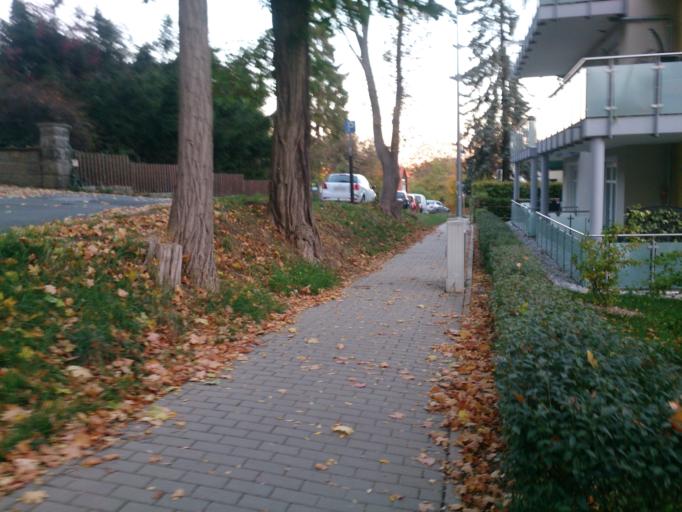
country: DE
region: Saxony-Anhalt
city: Wernigerode
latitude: 51.8285
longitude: 10.7785
